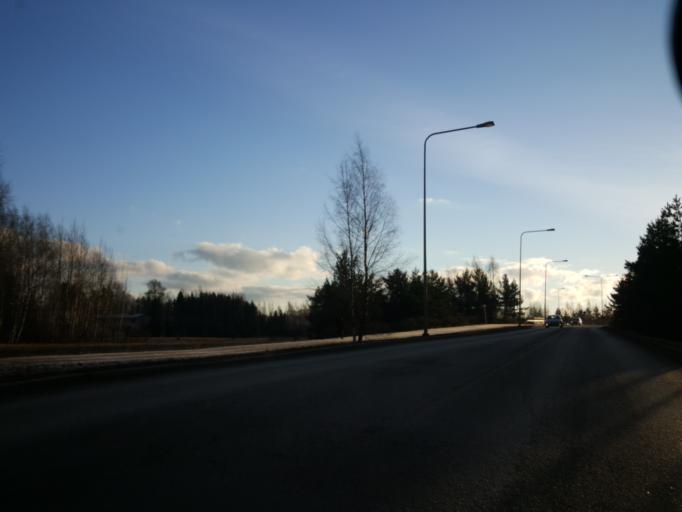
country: FI
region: Uusimaa
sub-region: Helsinki
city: Vantaa
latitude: 60.2435
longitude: 24.9792
